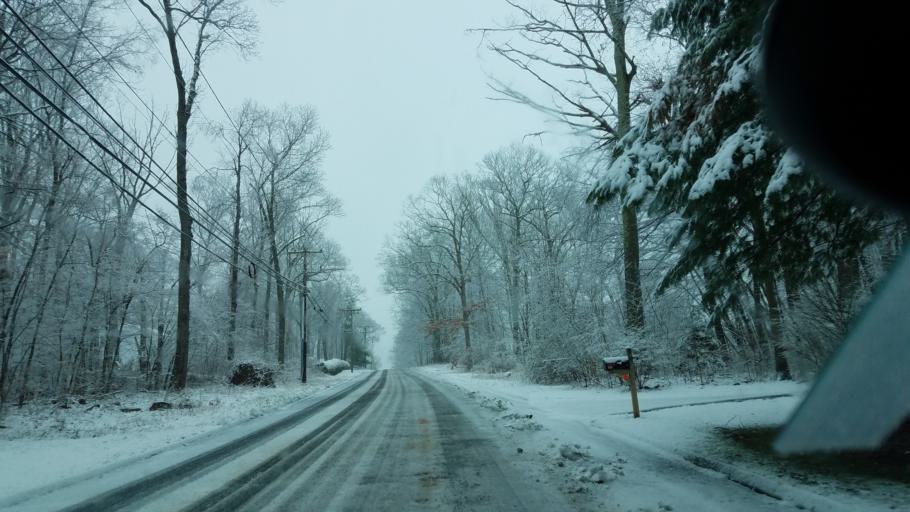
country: US
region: Connecticut
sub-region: New Haven County
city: Cheshire
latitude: 41.4890
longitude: -72.9312
